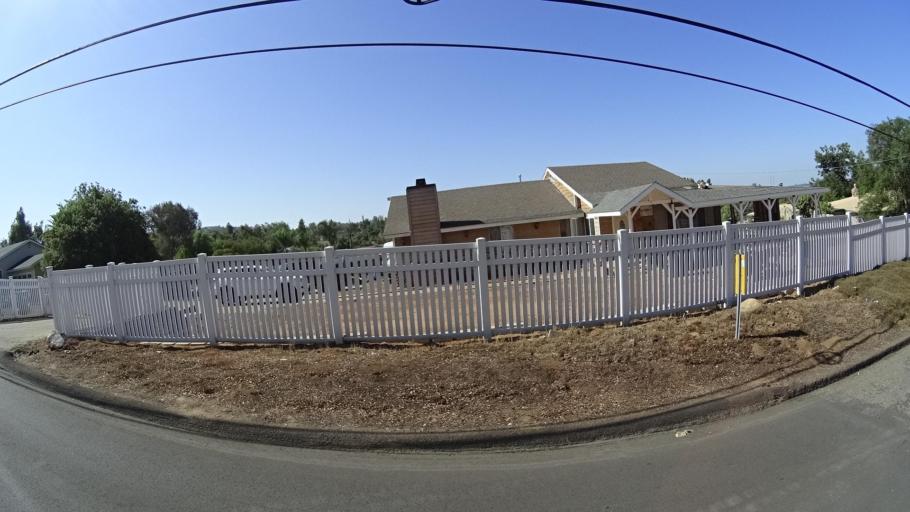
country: US
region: California
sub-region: San Diego County
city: Granite Hills
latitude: 32.7961
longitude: -116.9093
